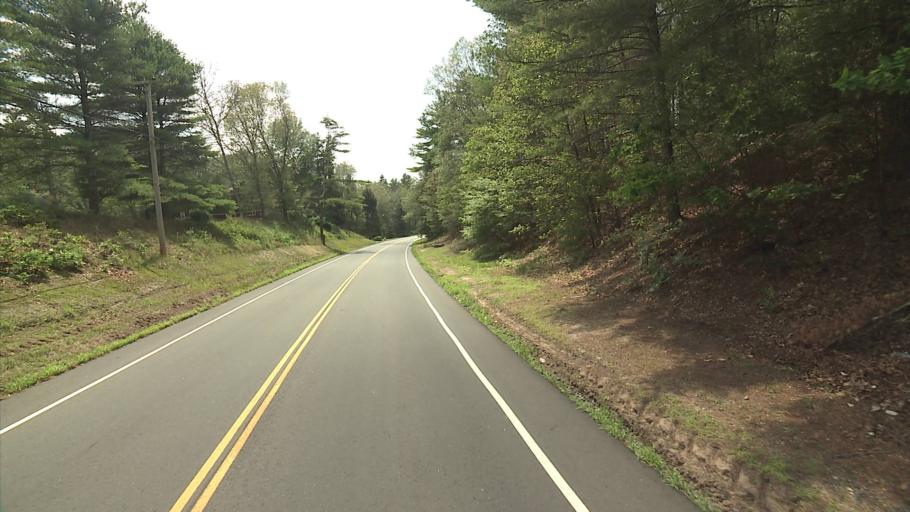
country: US
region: Connecticut
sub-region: New London County
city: Preston City
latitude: 41.5618
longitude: -71.8698
